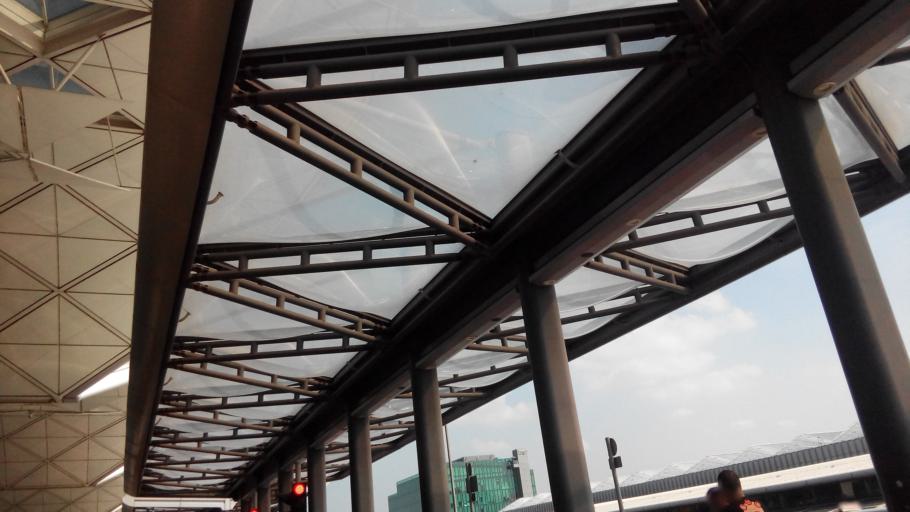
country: HK
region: Tuen Mun
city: Tuen Mun
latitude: 22.3149
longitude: 113.9366
